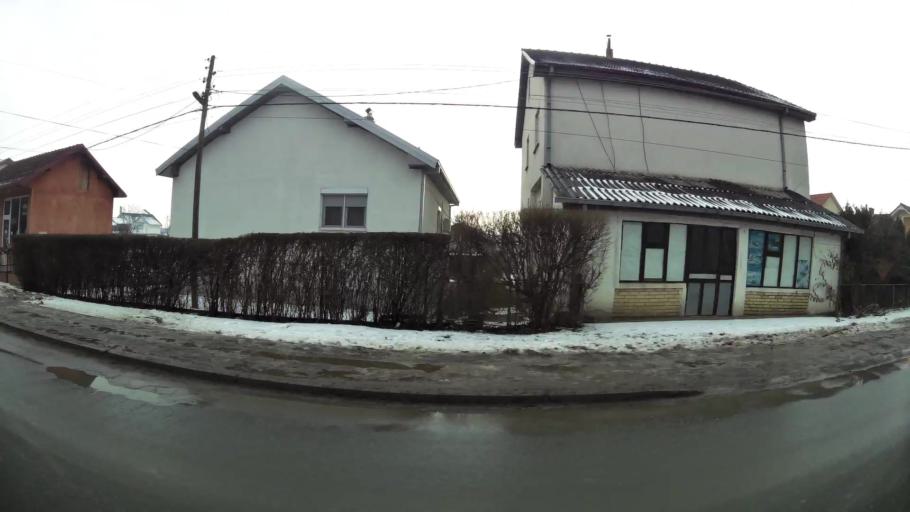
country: MK
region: Ilinden
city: Ilinden
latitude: 41.9969
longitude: 21.5783
